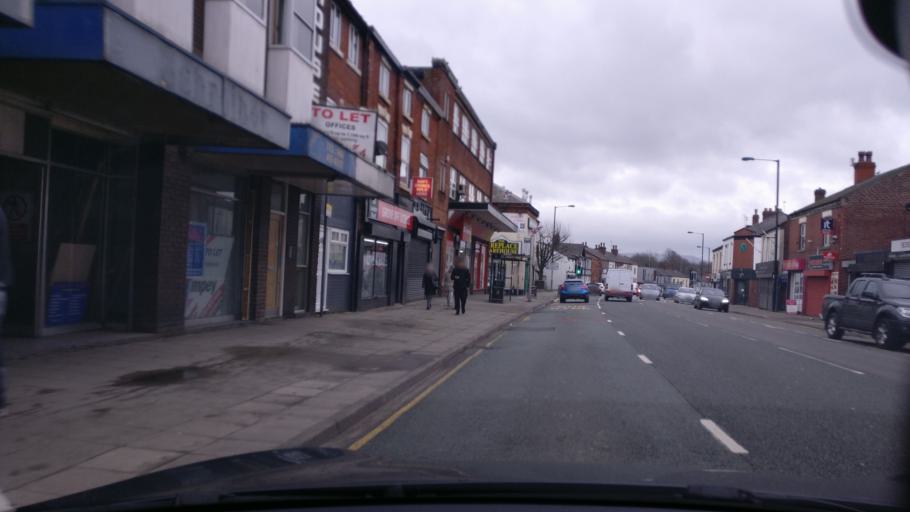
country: GB
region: England
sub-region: Borough of Stockport
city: Hazel Grove
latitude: 53.3795
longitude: -2.1203
